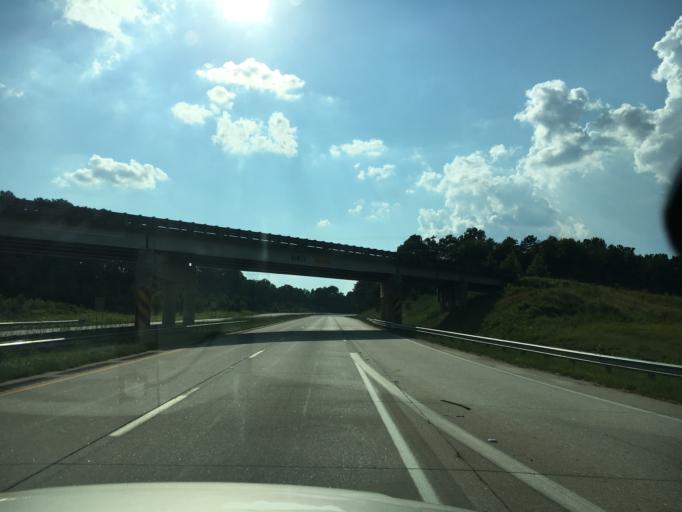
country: US
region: South Carolina
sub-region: Laurens County
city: Clinton
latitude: 34.5179
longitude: -81.8996
